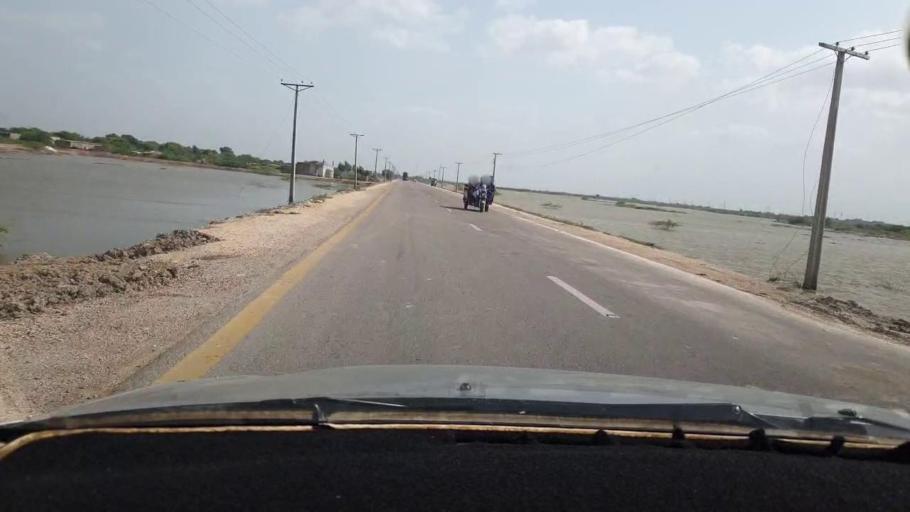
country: PK
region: Sindh
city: Naukot
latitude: 24.9306
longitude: 69.3169
